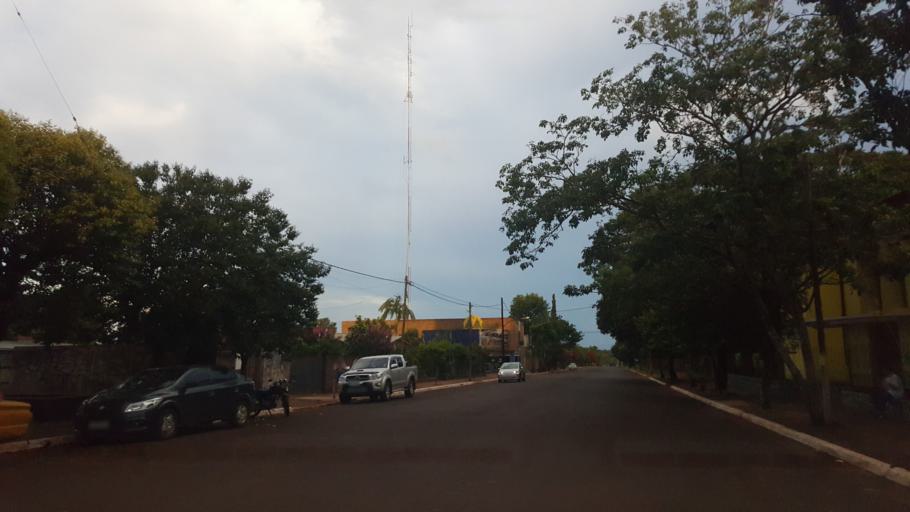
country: AR
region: Misiones
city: Jardin America
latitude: -27.0432
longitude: -55.2263
